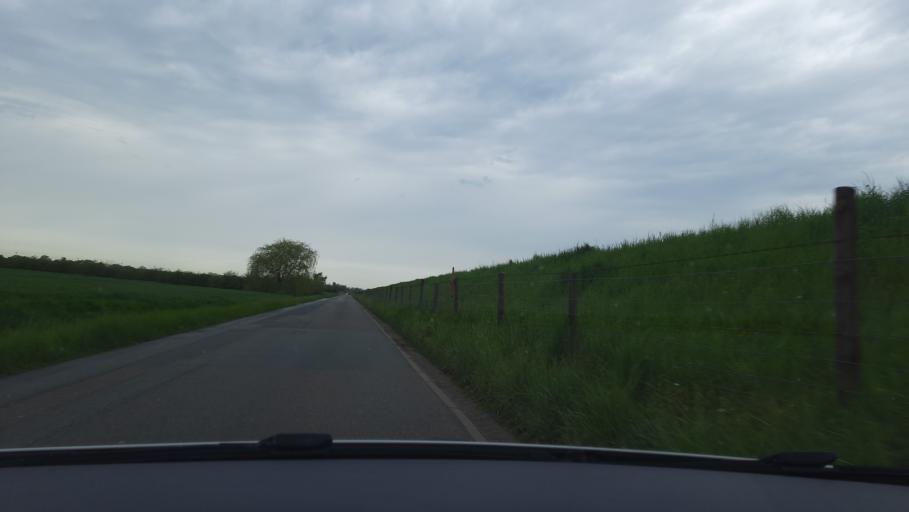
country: DE
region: Lower Saxony
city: Thedinghausen
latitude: 52.9827
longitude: 9.0408
